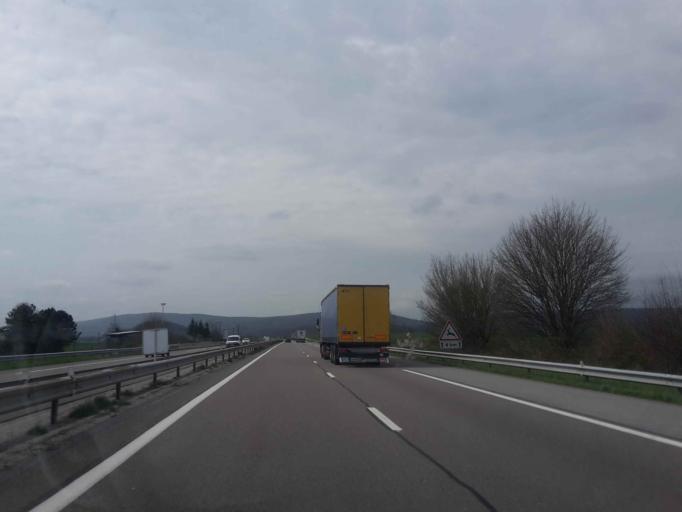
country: FR
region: Franche-Comte
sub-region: Departement du Doubs
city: Roulans
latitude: 47.3380
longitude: 6.2133
